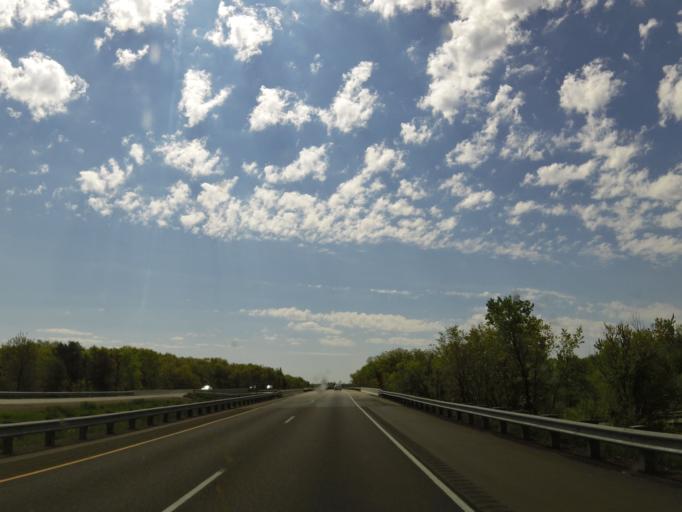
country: US
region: Wisconsin
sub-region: Eau Claire County
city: Fall Creek
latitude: 44.6801
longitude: -91.3273
